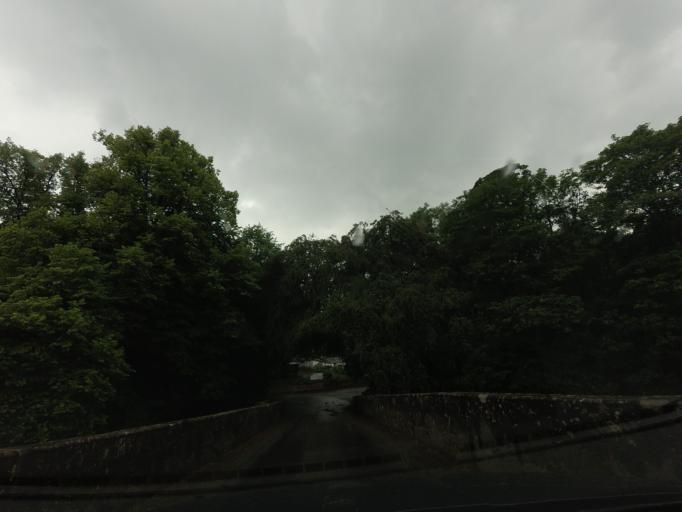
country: GB
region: Scotland
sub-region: Dumfries and Galloway
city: Annan
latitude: 55.0418
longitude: -3.3105
